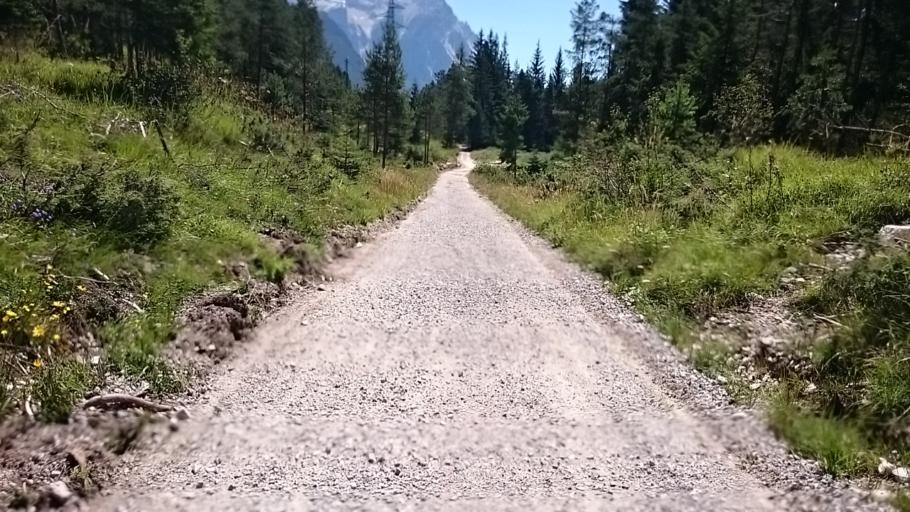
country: IT
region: Veneto
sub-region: Provincia di Belluno
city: Cortina d'Ampezzo
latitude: 46.4989
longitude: 12.1674
